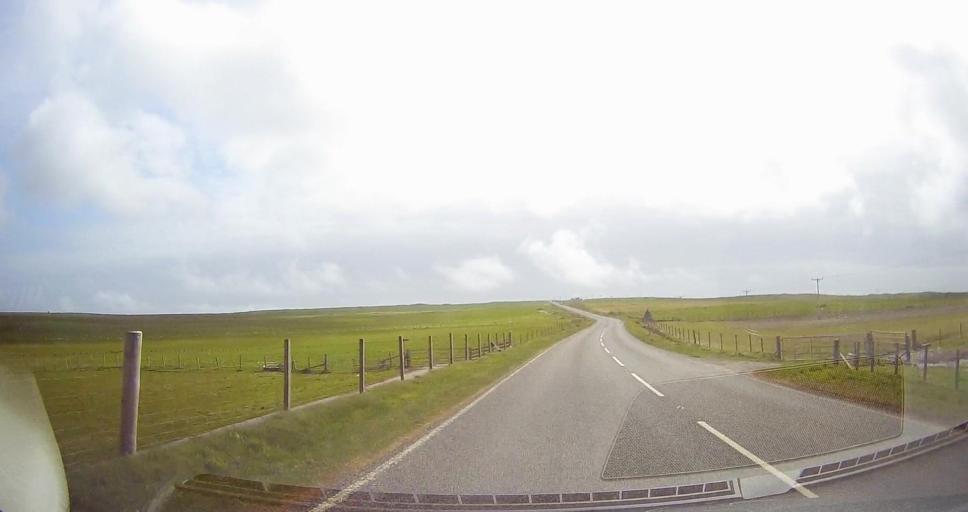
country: GB
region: Scotland
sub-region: Shetland Islands
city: Sandwick
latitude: 59.9090
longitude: -1.3016
